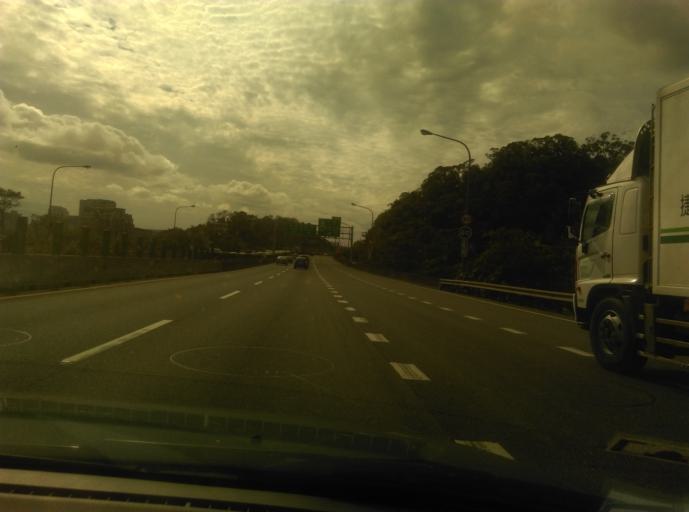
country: TW
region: Taiwan
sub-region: Keelung
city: Keelung
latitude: 25.0779
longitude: 121.6622
